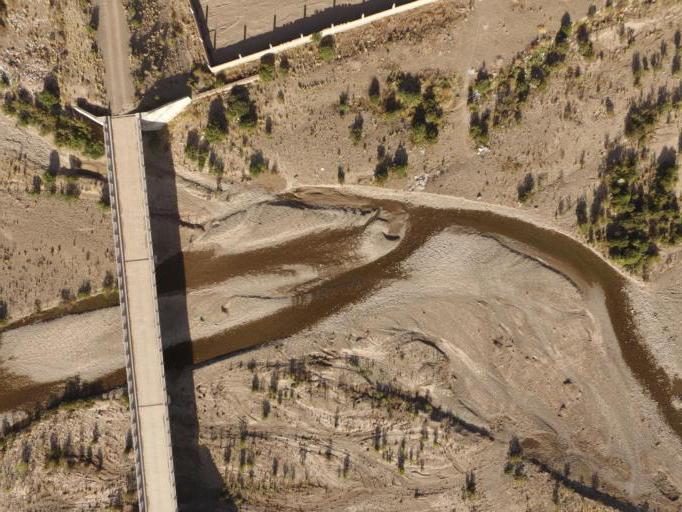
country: BO
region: Oruro
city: Challapata
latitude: -18.6909
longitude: -66.7586
